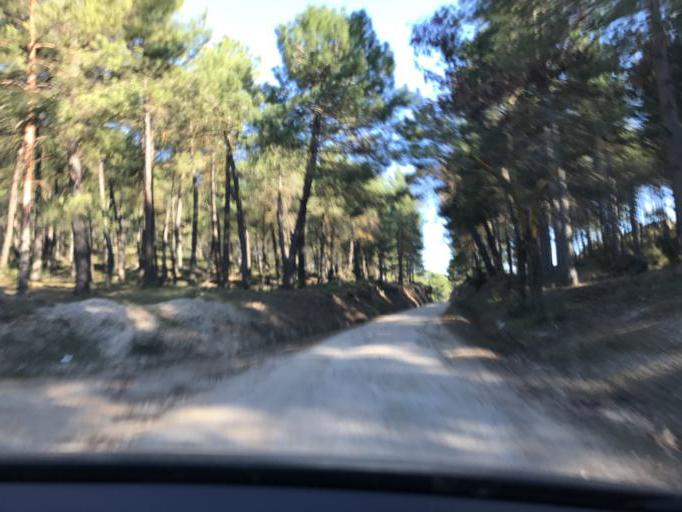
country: ES
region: Andalusia
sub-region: Provincia de Granada
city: Beas de Granada
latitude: 37.2533
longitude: -3.4670
